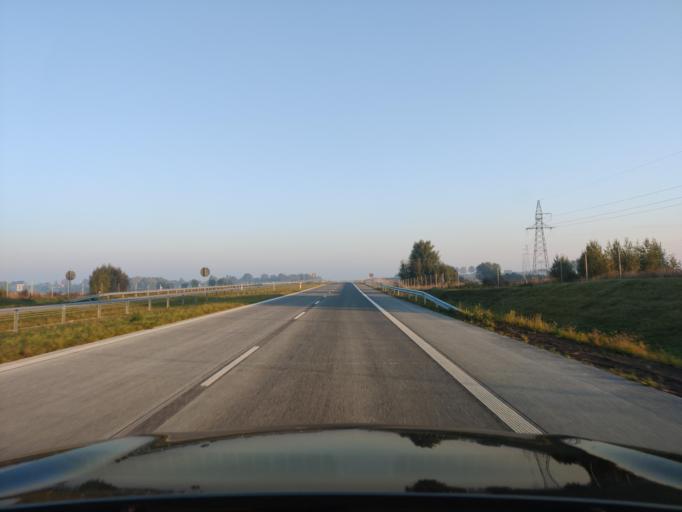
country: PL
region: Masovian Voivodeship
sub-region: Powiat mlawski
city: Mlawa
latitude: 53.1083
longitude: 20.4119
